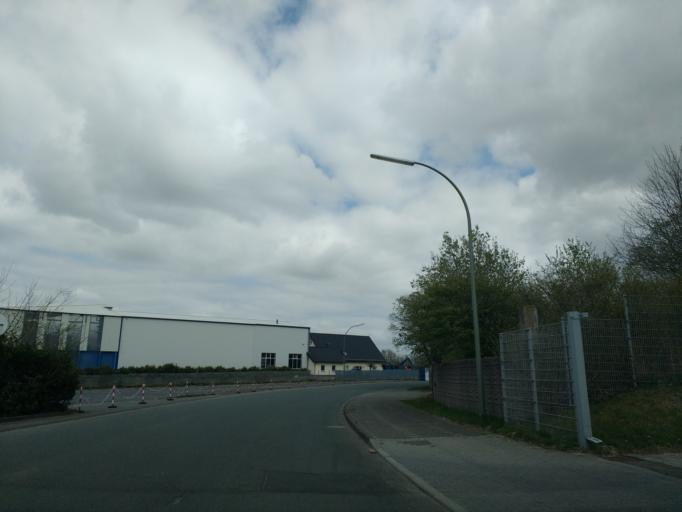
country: DE
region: North Rhine-Westphalia
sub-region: Regierungsbezirk Detmold
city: Wunnenberg
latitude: 51.5786
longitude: 8.7189
